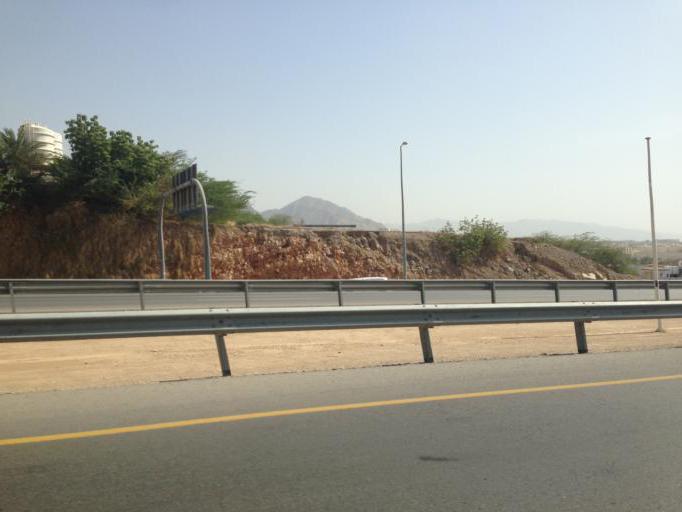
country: OM
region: Muhafazat Masqat
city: Bawshar
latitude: 23.5693
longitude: 58.4038
